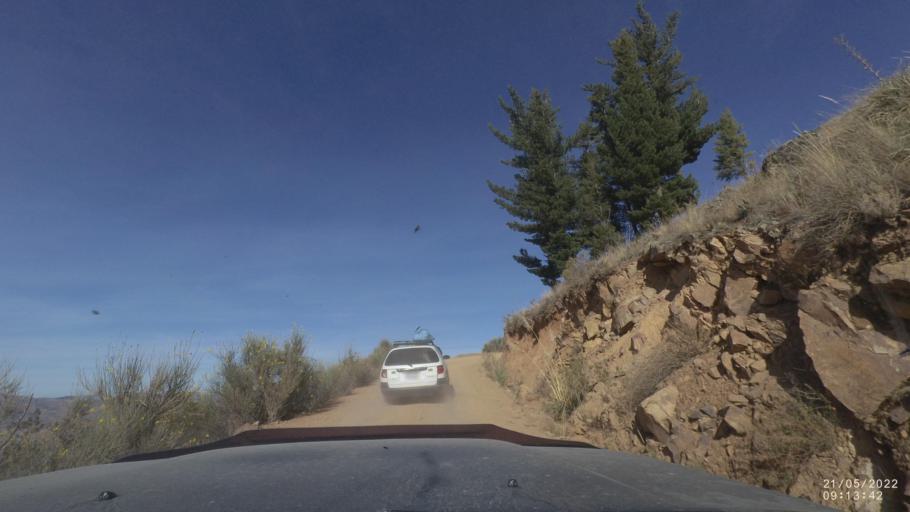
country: BO
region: Cochabamba
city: Cochabamba
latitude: -17.3666
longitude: -66.0273
